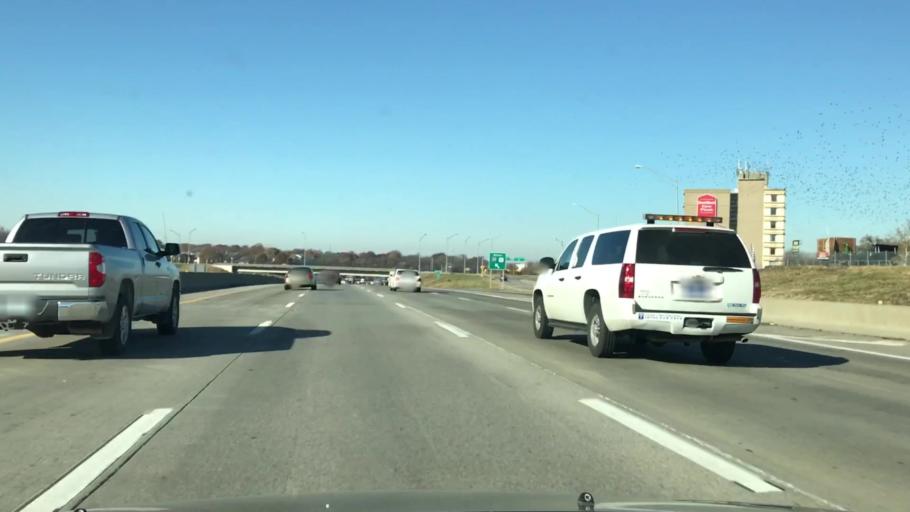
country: US
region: Missouri
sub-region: Jackson County
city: Grandview
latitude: 38.9136
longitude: -94.5252
